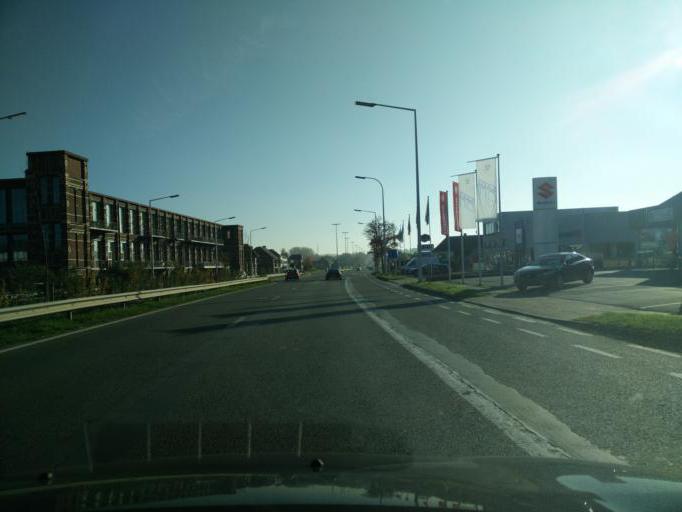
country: BE
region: Flanders
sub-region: Provincie Oost-Vlaanderen
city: Oudenaarde
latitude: 50.8292
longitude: 3.6036
